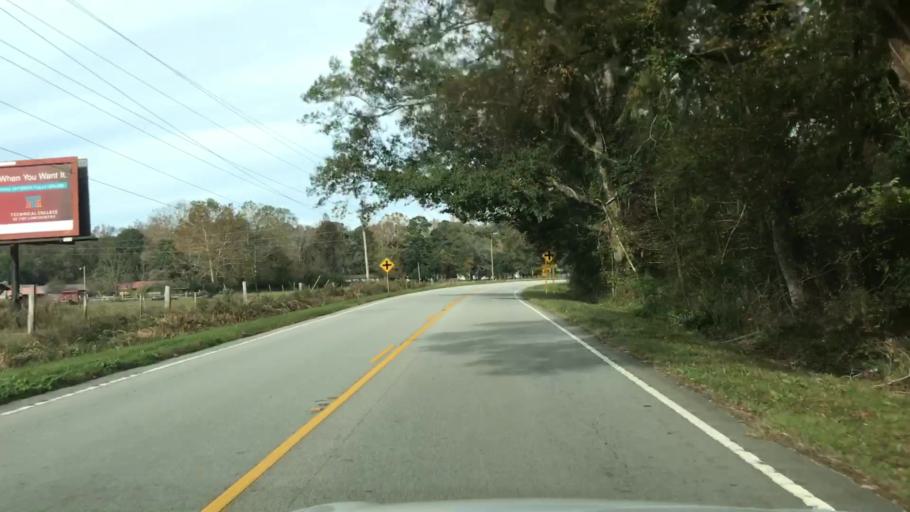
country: US
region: South Carolina
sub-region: Colleton County
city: Walterboro
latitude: 32.8226
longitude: -80.5553
